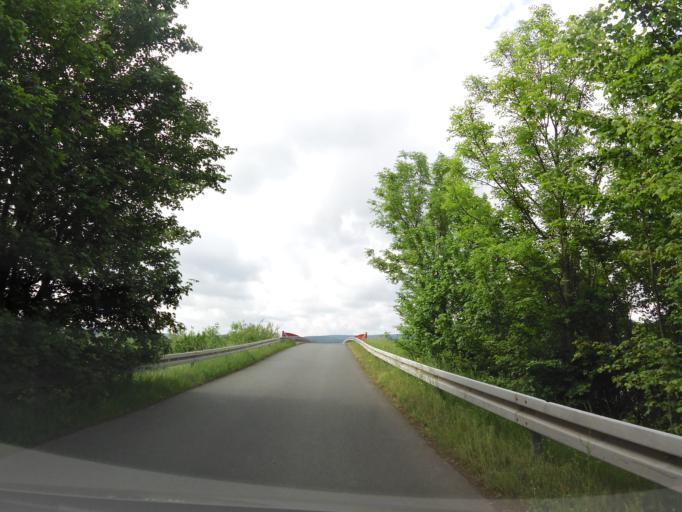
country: DE
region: Thuringia
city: Horselgau
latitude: 50.9079
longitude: 10.5986
